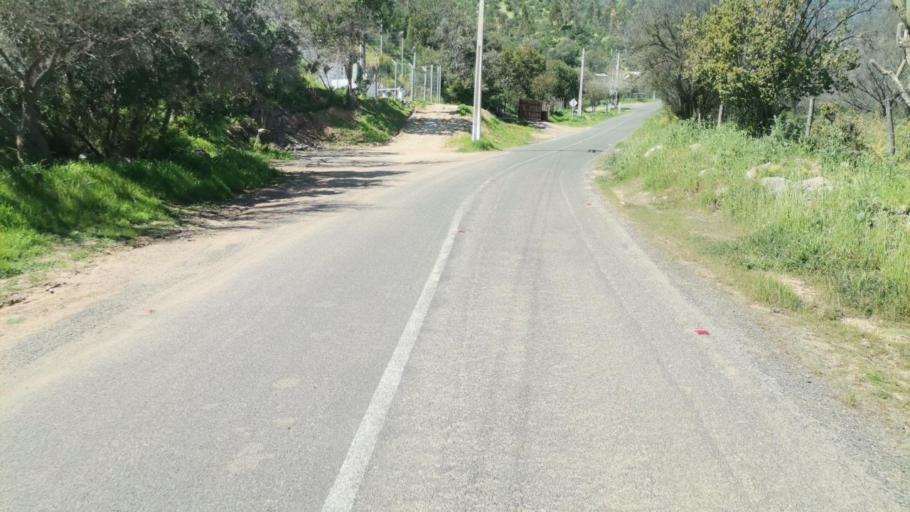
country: CL
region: Valparaiso
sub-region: Provincia de Marga Marga
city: Limache
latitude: -33.1837
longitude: -71.1070
